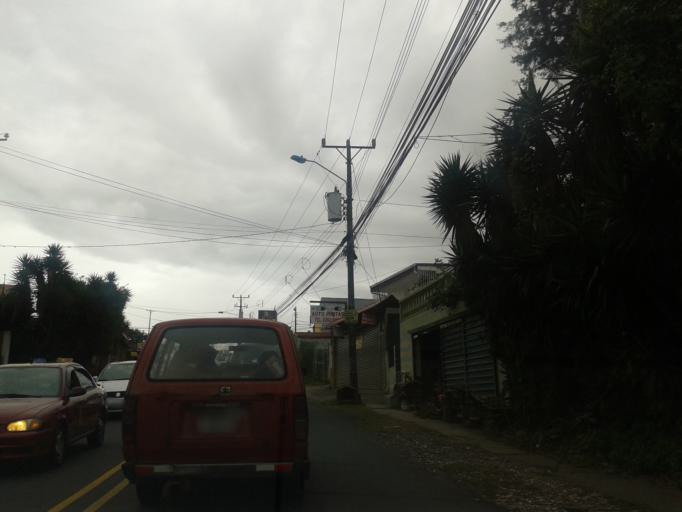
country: CR
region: Heredia
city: San Pablo
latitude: 9.9922
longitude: -84.1032
